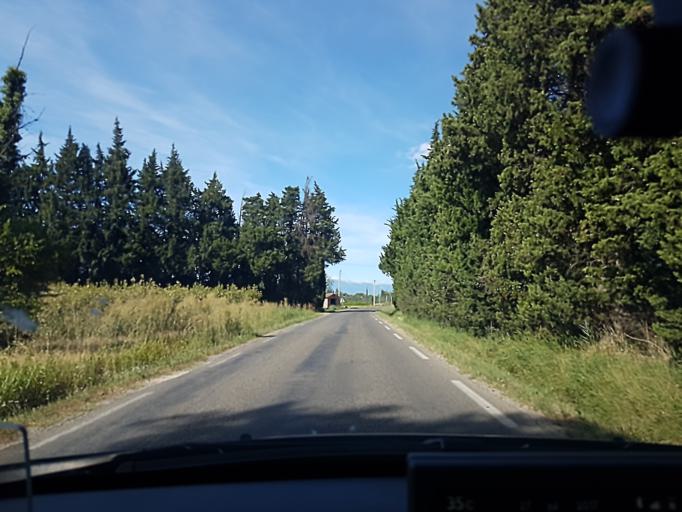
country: FR
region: Provence-Alpes-Cote d'Azur
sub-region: Departement du Vaucluse
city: Caumont-sur-Durance
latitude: 43.9094
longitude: 4.9645
